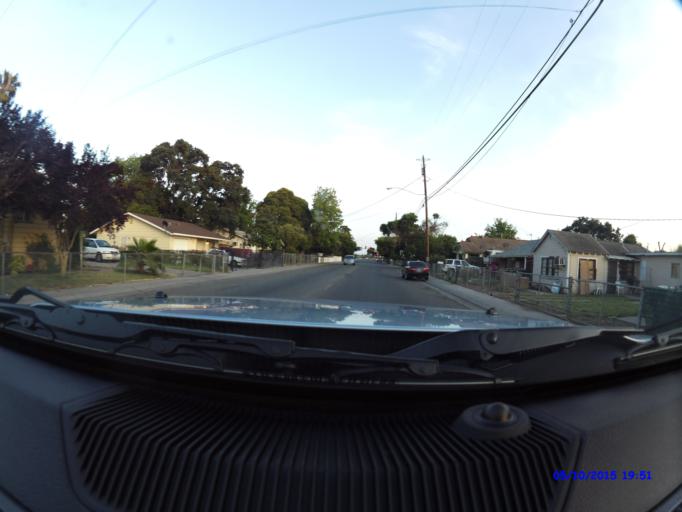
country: US
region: California
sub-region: San Joaquin County
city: Garden Acres
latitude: 37.9530
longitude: -121.2439
